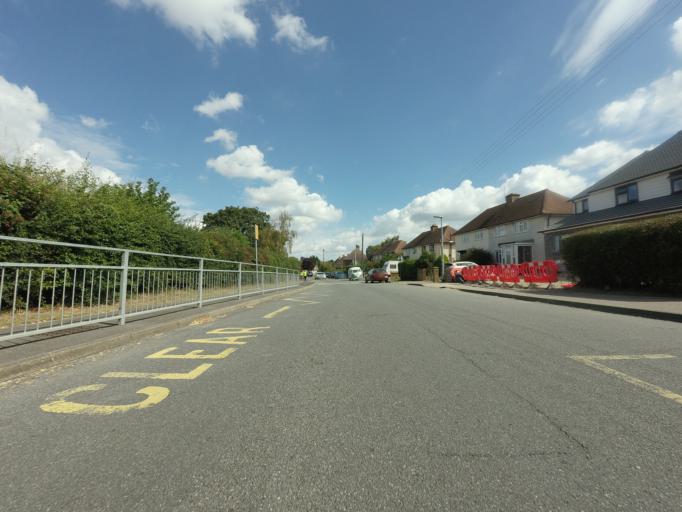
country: GB
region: England
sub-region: Medway
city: High Halstow
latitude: 51.4498
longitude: 0.5628
